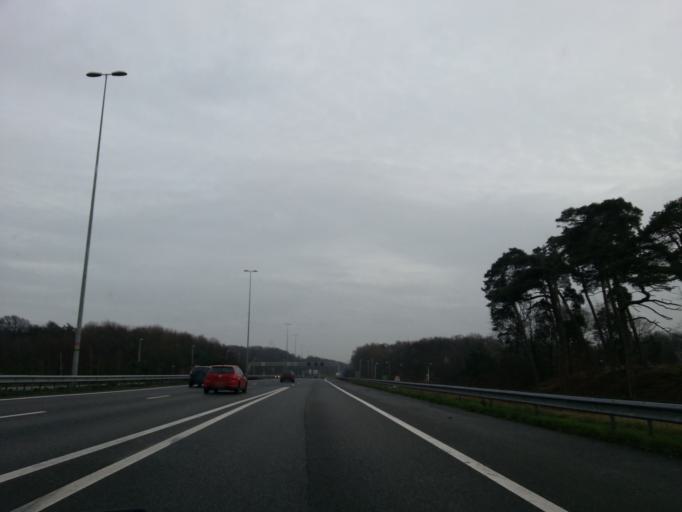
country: NL
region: Gelderland
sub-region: Gemeente Arnhem
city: Arnhem
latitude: 52.0158
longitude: 5.9234
